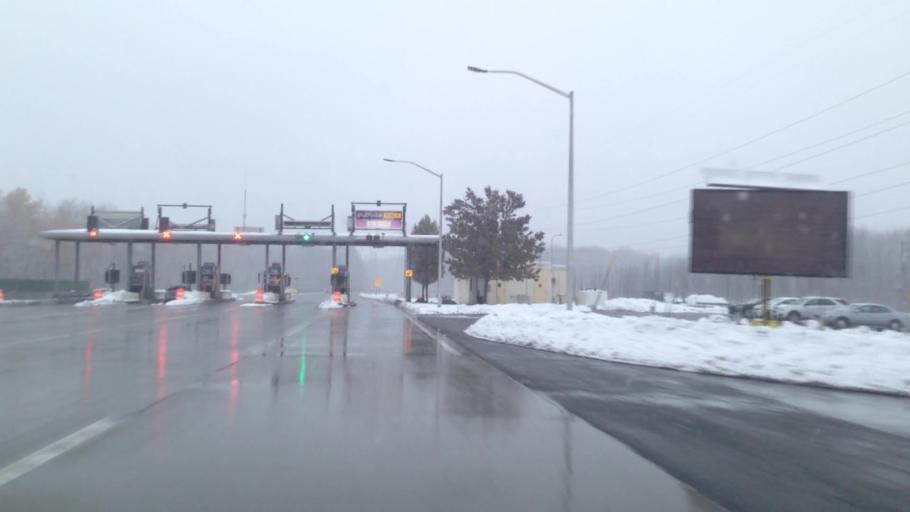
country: US
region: New York
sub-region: Onondaga County
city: East Syracuse
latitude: 43.0983
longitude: -76.0488
